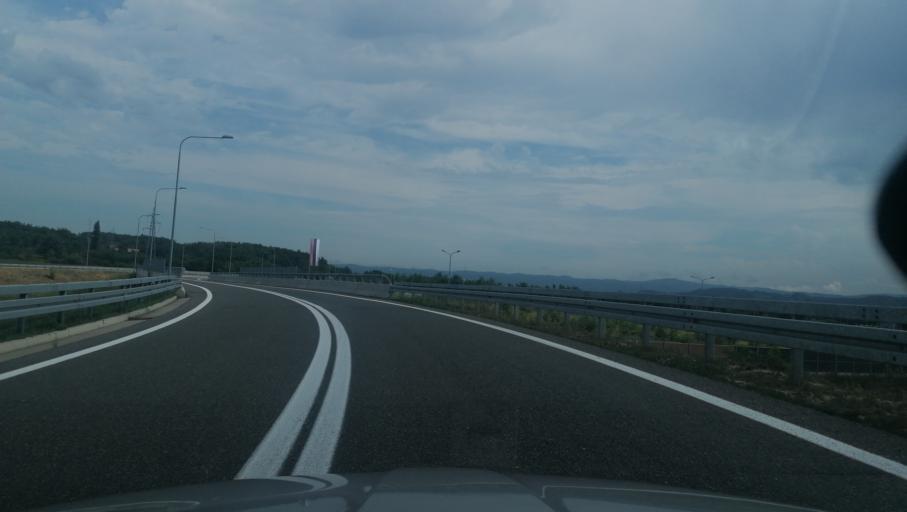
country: BA
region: Republika Srpska
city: Doboj
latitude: 44.8094
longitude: 18.0406
